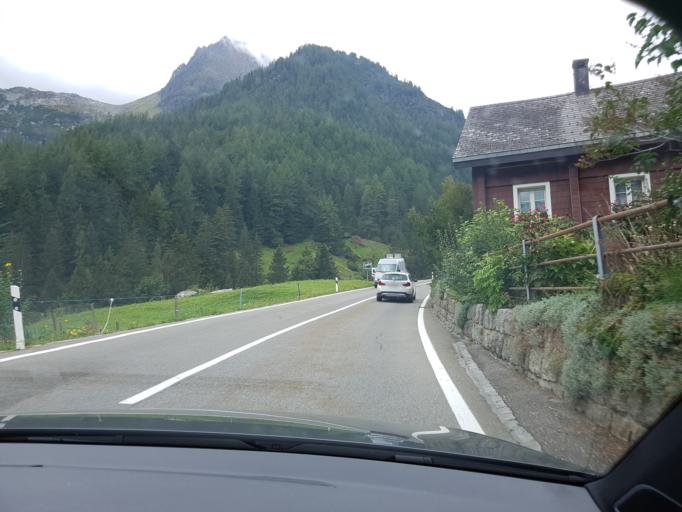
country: CH
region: Uri
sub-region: Uri
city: Andermatt
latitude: 46.7233
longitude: 8.5576
